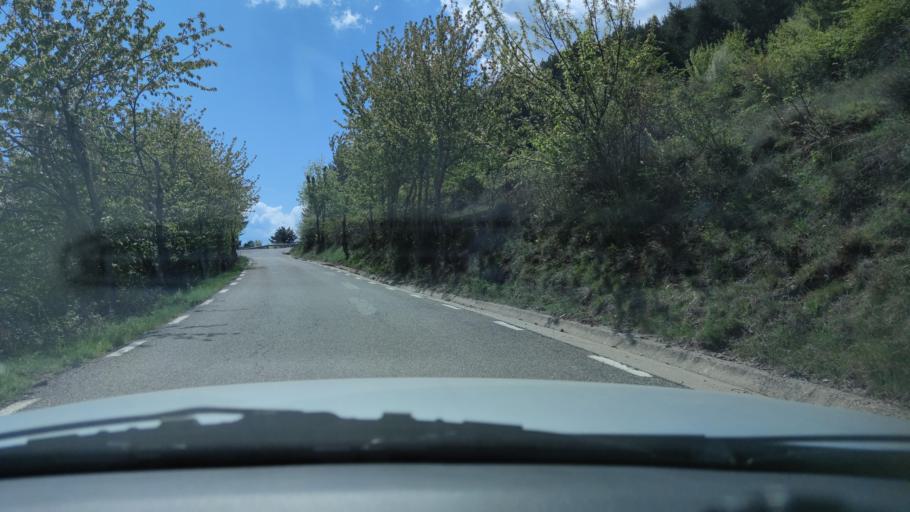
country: ES
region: Catalonia
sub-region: Provincia de Lleida
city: Coll de Nargo
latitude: 42.3095
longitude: 1.2812
